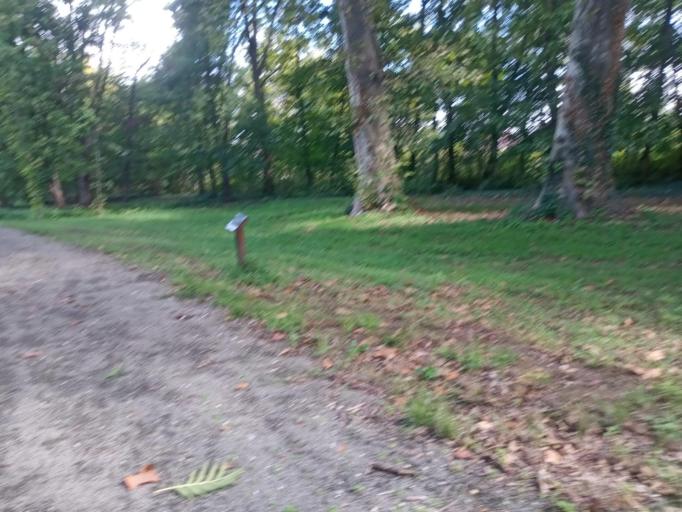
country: HU
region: Veszprem
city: Osi
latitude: 47.1364
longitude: 18.2466
